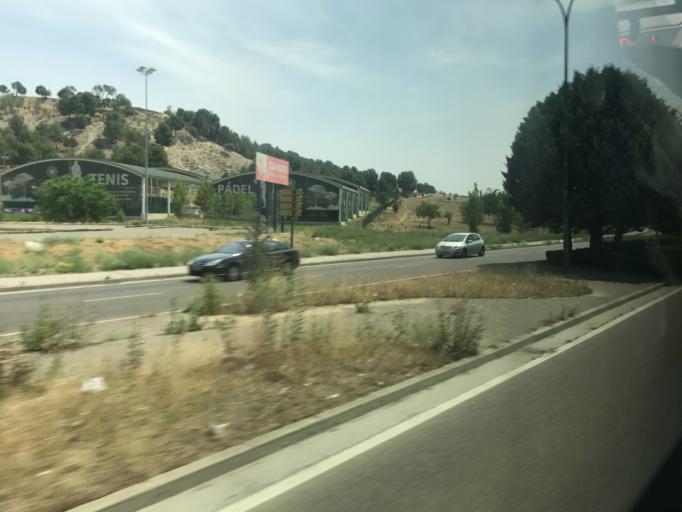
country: ES
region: Castille and Leon
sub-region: Provincia de Valladolid
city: Zaratan
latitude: 41.6485
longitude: -4.7576
